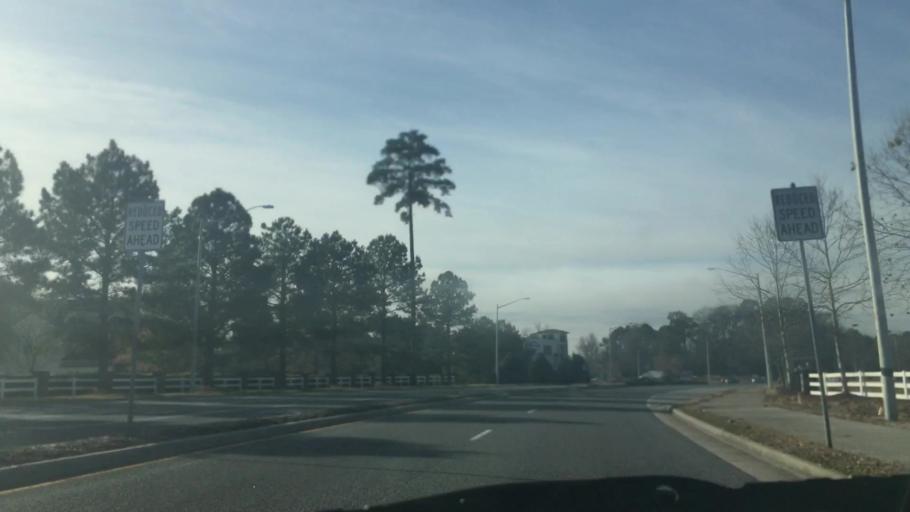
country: US
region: Virginia
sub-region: City of Chesapeake
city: Chesapeake
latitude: 36.8059
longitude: -76.1307
